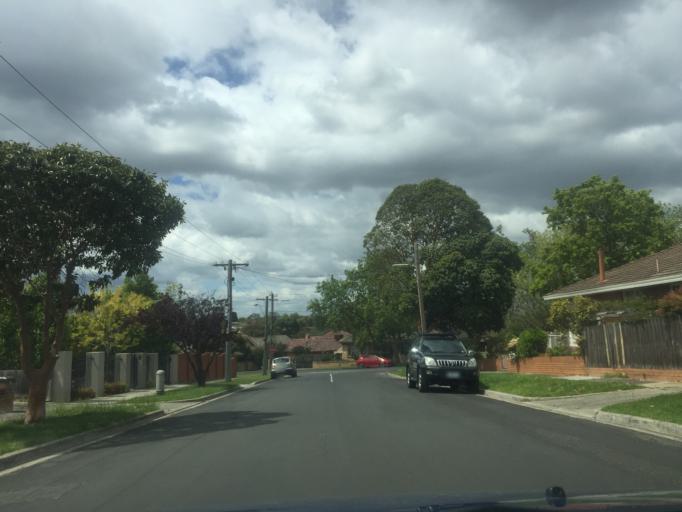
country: AU
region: Victoria
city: Alphington
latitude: -37.7935
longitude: 145.0371
